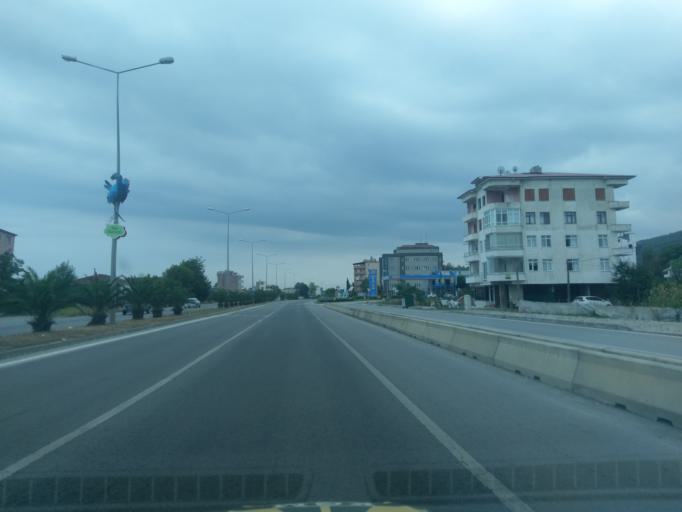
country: TR
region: Samsun
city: Taflan
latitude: 41.4016
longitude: 36.1895
